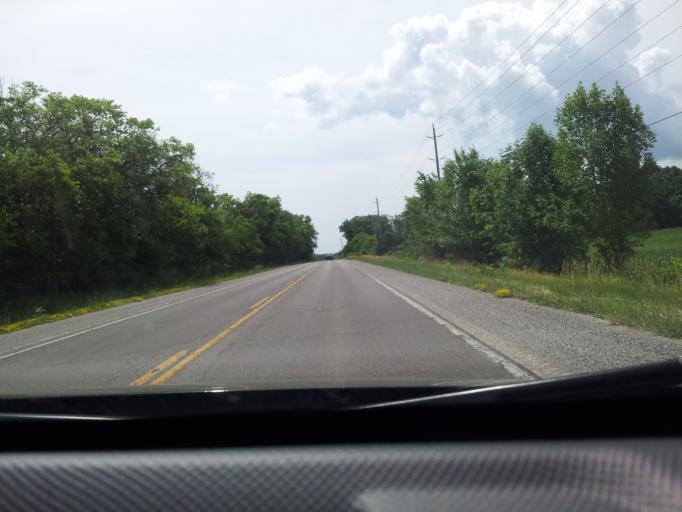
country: CA
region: Ontario
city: Norfolk County
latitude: 42.8161
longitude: -80.2504
